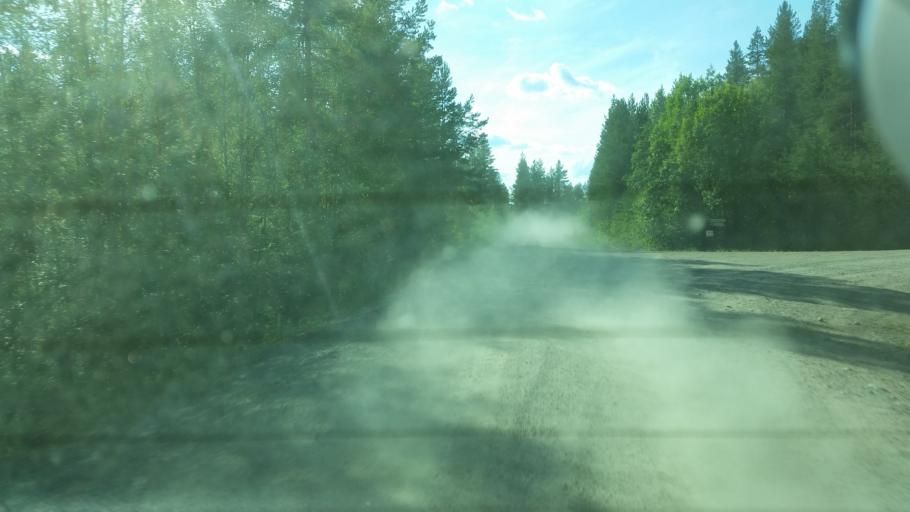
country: SE
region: Vaesternorrland
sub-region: Ange Kommun
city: Ange
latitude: 62.2006
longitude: 15.5649
